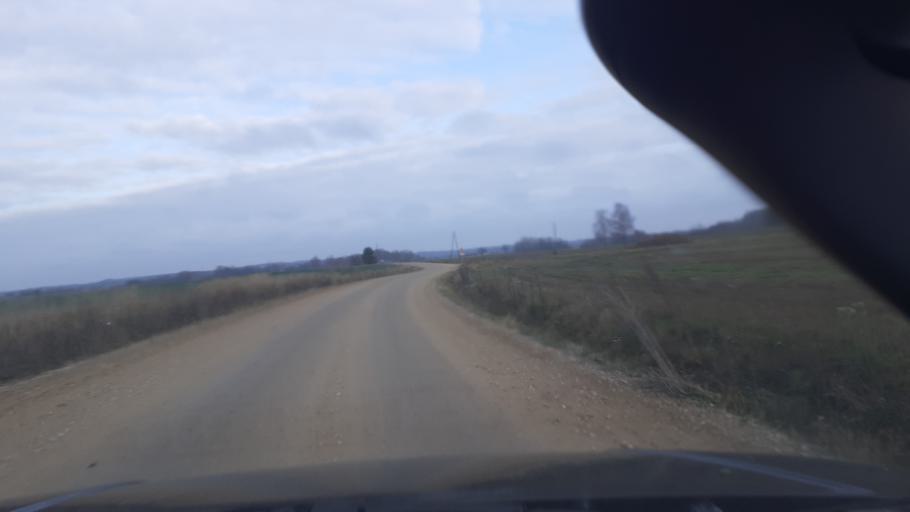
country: LV
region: Aizpute
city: Aizpute
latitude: 56.8512
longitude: 21.6663
